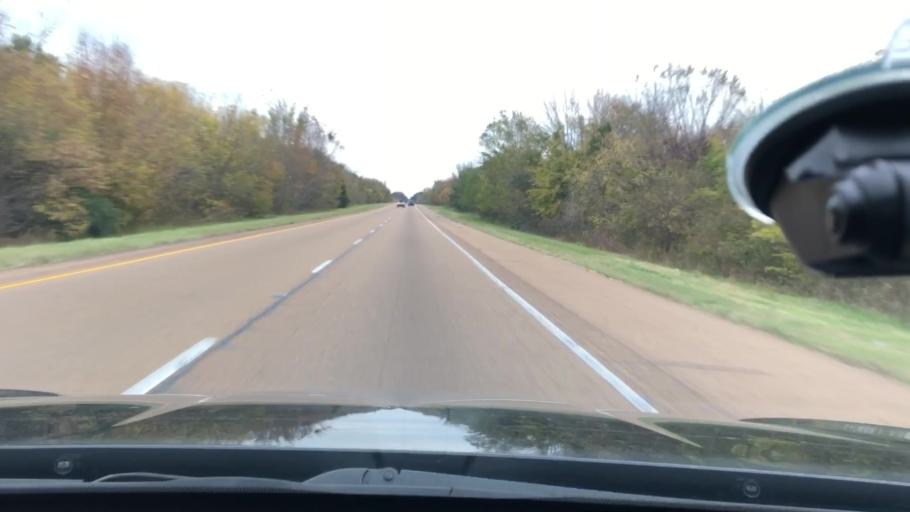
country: US
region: Arkansas
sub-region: Hempstead County
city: Hope
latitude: 33.7517
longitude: -93.5037
